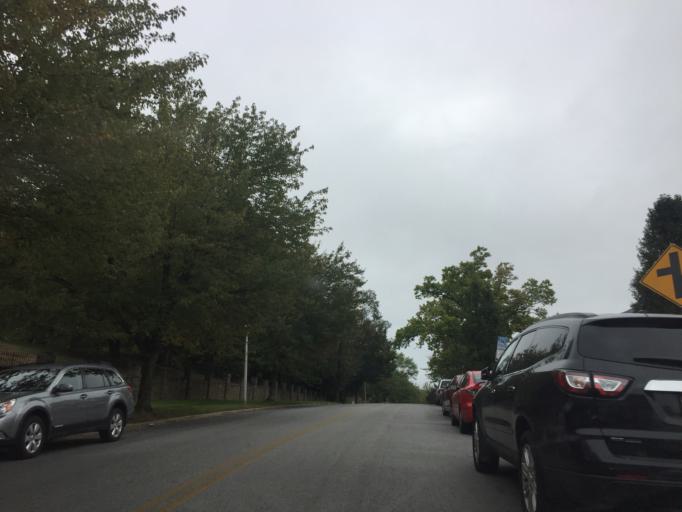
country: US
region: Maryland
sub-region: City of Baltimore
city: Baltimore
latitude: 39.3351
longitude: -76.6051
